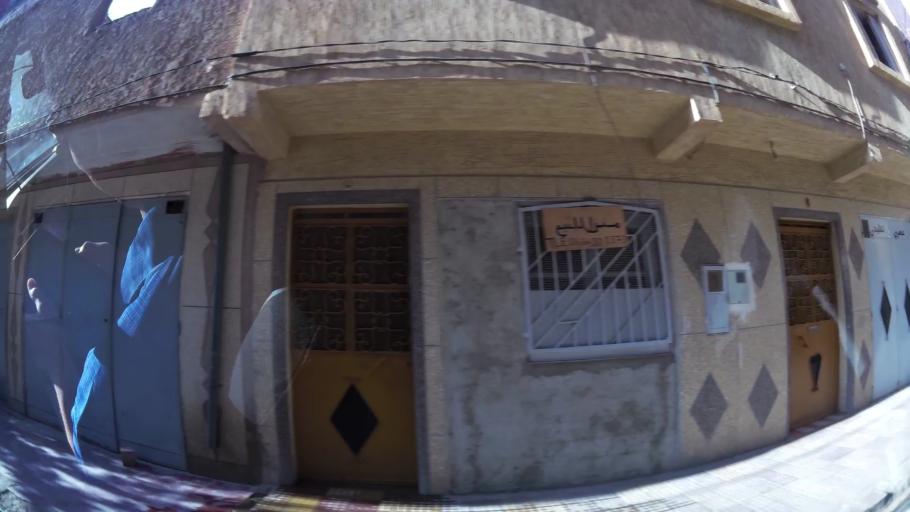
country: MA
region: Oriental
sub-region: Oujda-Angad
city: Oujda
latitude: 34.7103
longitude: -1.8970
